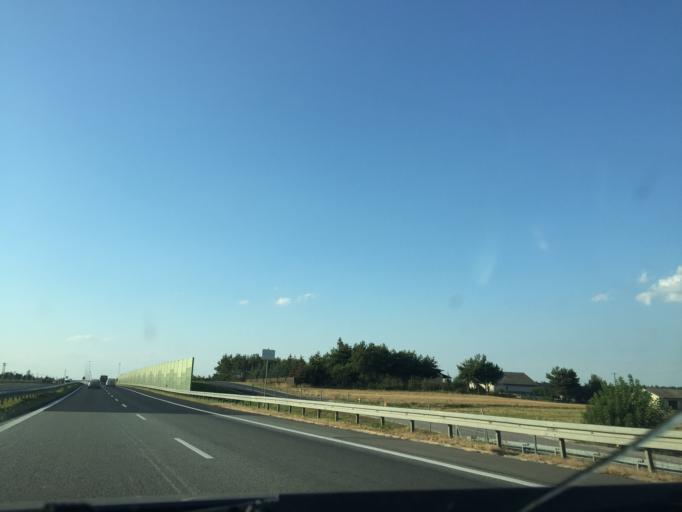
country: PL
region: Masovian Voivodeship
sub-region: Powiat bialobrzeski
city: Promna
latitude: 51.6869
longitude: 20.9355
